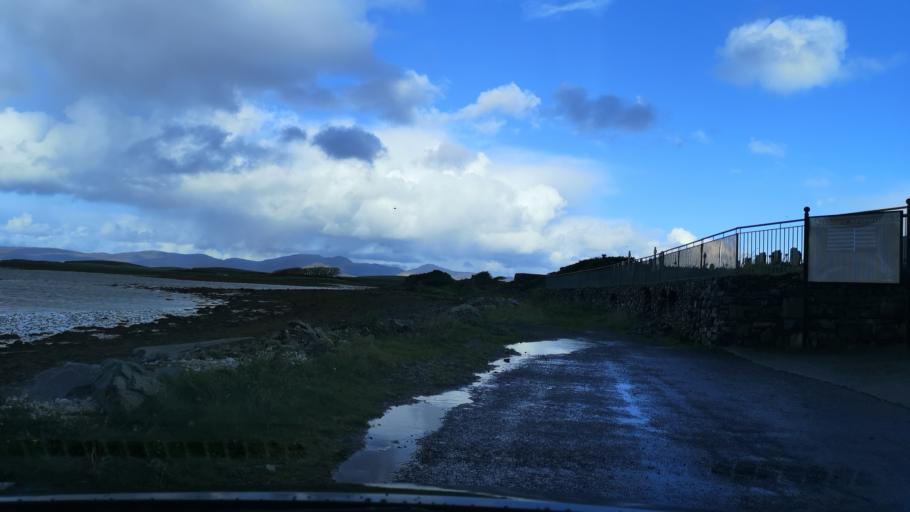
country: IE
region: Connaught
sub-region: Maigh Eo
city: Westport
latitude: 53.7827
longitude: -9.6400
